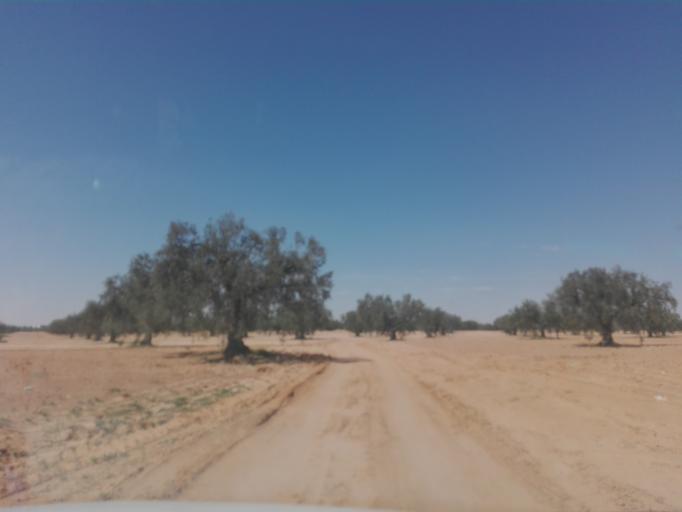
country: TN
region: Safaqis
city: Bi'r `Ali Bin Khalifah
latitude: 34.6624
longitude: 10.3188
